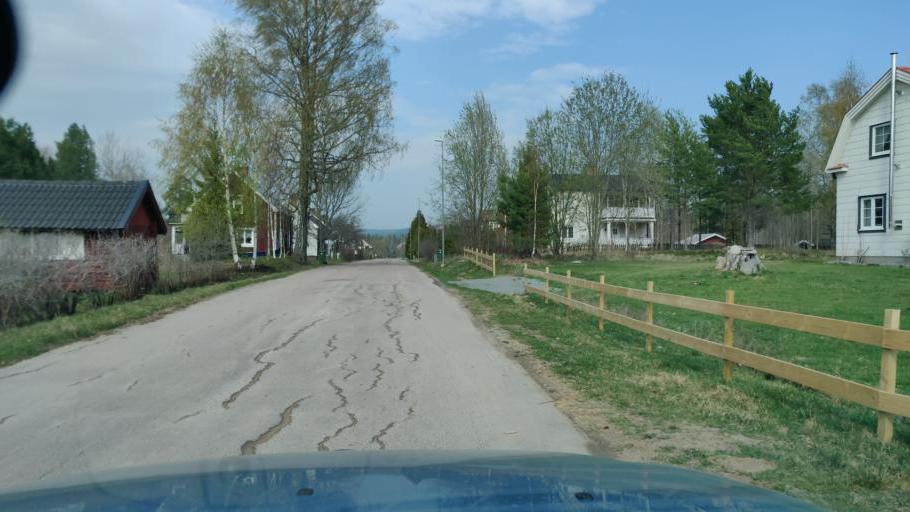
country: SE
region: Vaermland
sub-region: Munkfors Kommun
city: Munkfors
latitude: 59.8404
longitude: 13.5608
